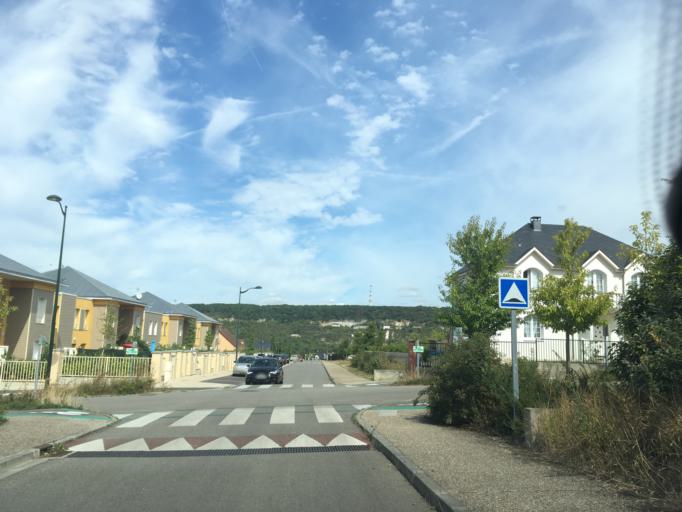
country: FR
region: Haute-Normandie
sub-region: Departement de l'Eure
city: Vernon
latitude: 49.0804
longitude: 1.4970
